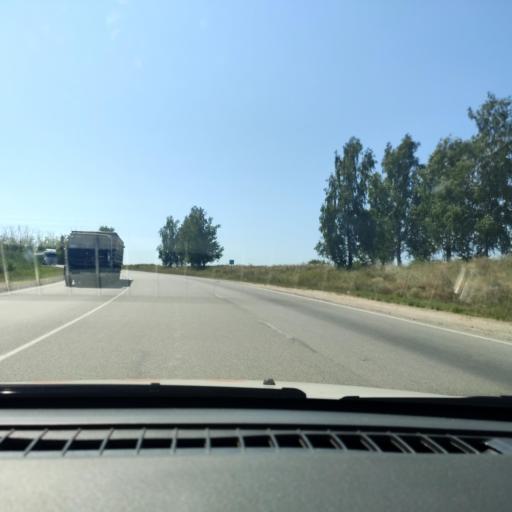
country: RU
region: Voronezj
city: Ostrogozhsk
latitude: 51.0210
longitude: 38.9811
